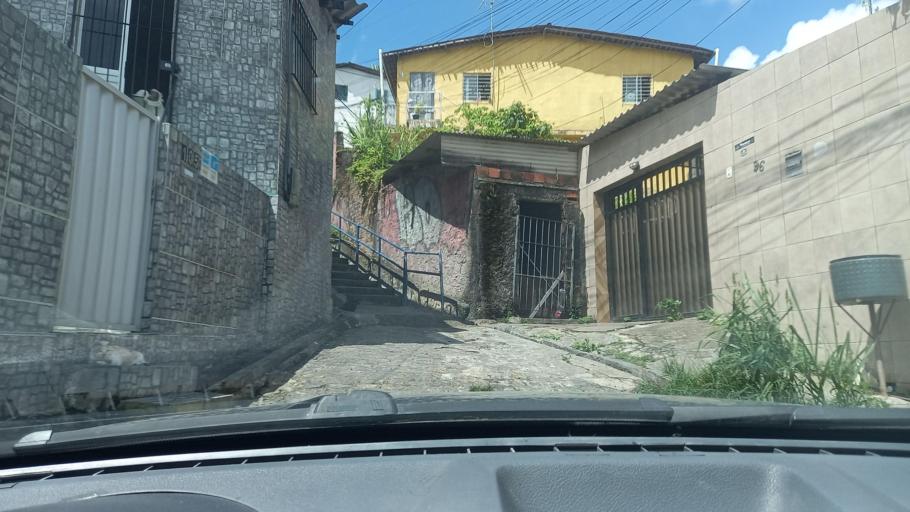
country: BR
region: Pernambuco
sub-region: Jaboatao Dos Guararapes
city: Jaboatao dos Guararapes
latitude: -8.1246
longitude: -34.9524
